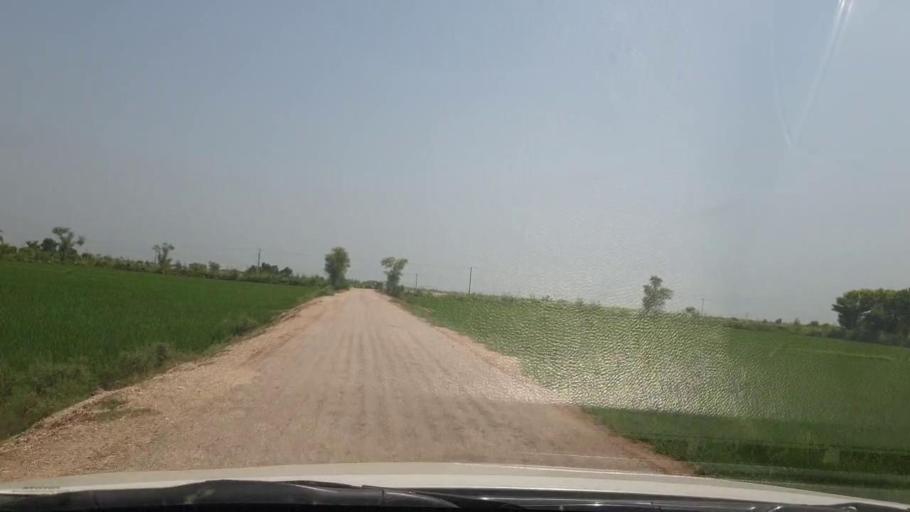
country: PK
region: Sindh
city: Rustam jo Goth
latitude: 28.0212
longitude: 68.8012
